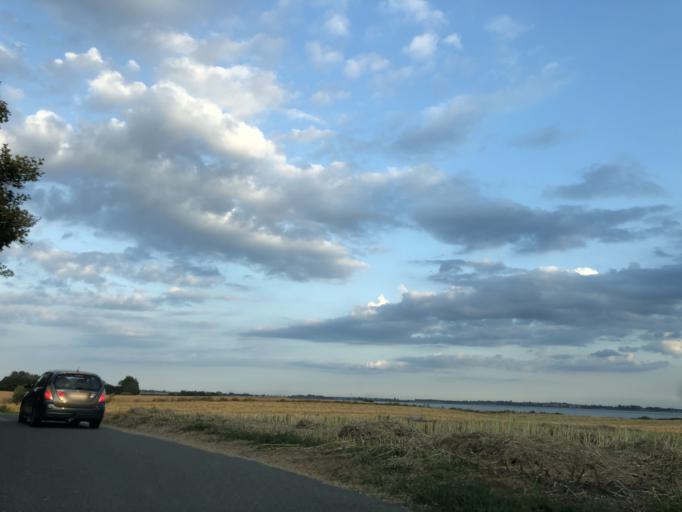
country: DK
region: South Denmark
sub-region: Kerteminde Kommune
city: Munkebo
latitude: 55.5141
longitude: 10.5952
